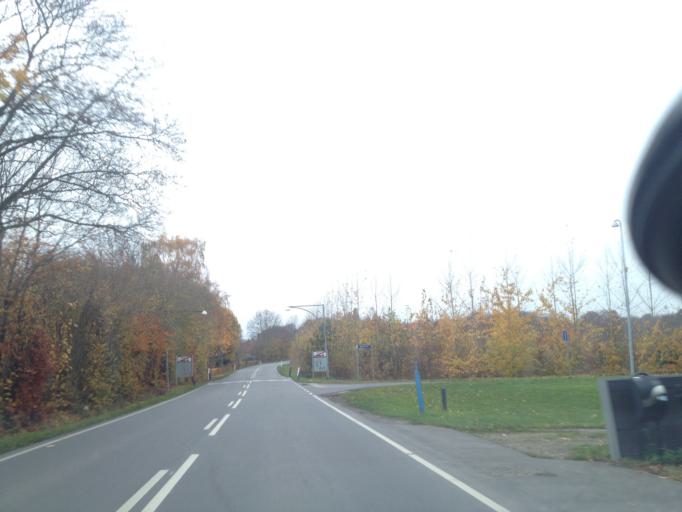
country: DK
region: South Denmark
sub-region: Assens Kommune
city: Vissenbjerg
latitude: 55.4429
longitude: 10.1792
